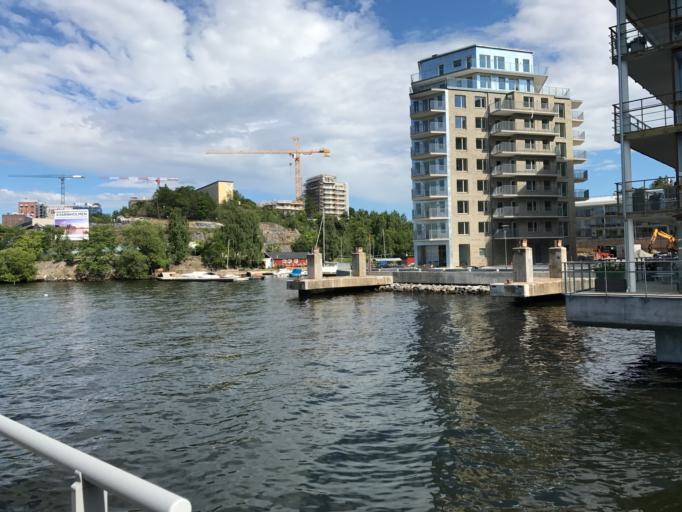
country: SE
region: Stockholm
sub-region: Nacka Kommun
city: Nacka
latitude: 59.3164
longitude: 18.1284
